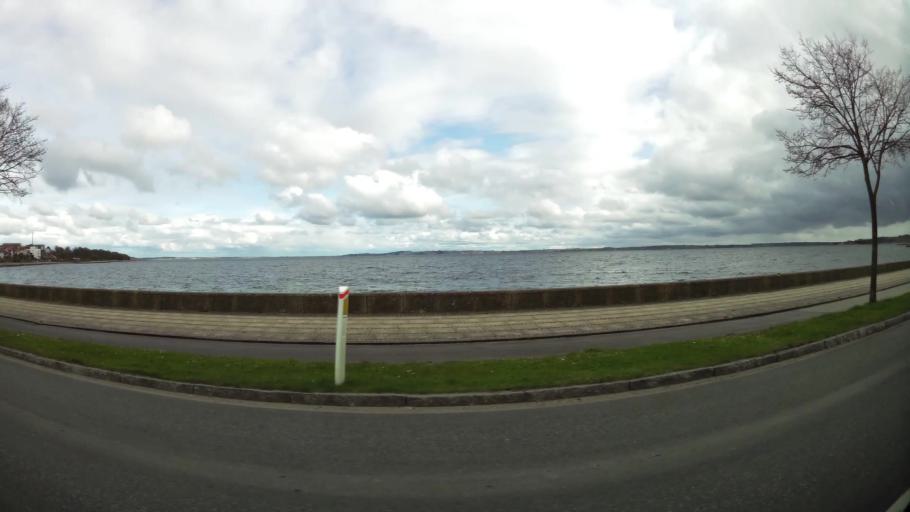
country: DK
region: North Denmark
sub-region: Thisted Kommune
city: Thisted
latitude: 56.9521
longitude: 8.6696
